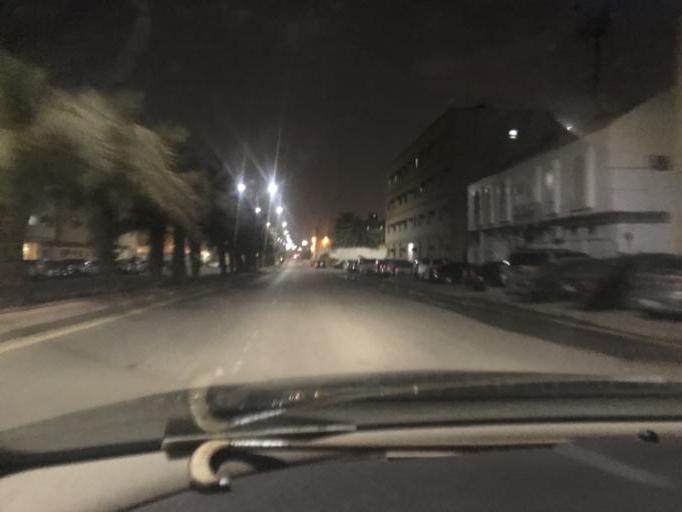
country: SA
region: Ar Riyad
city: Riyadh
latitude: 24.7336
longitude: 46.7817
